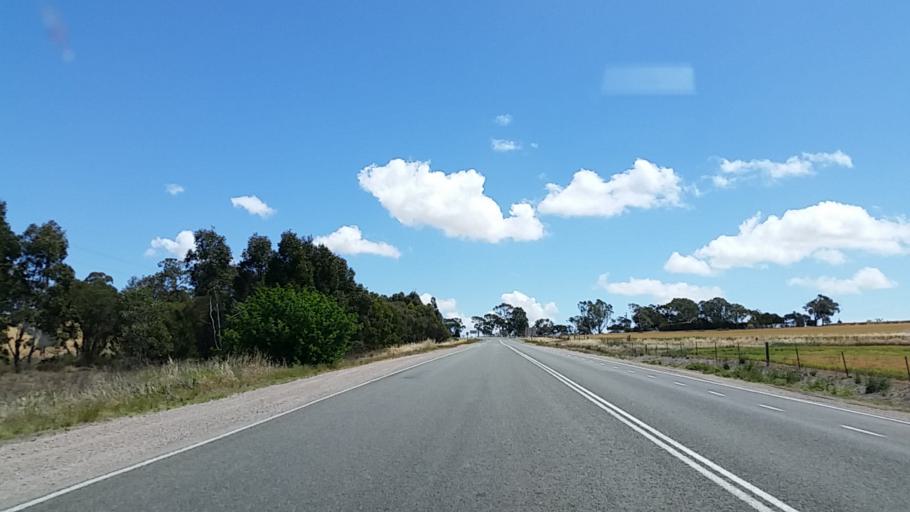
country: AU
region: South Australia
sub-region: Port Pirie City and Dists
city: Crystal Brook
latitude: -33.2828
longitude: 138.2675
